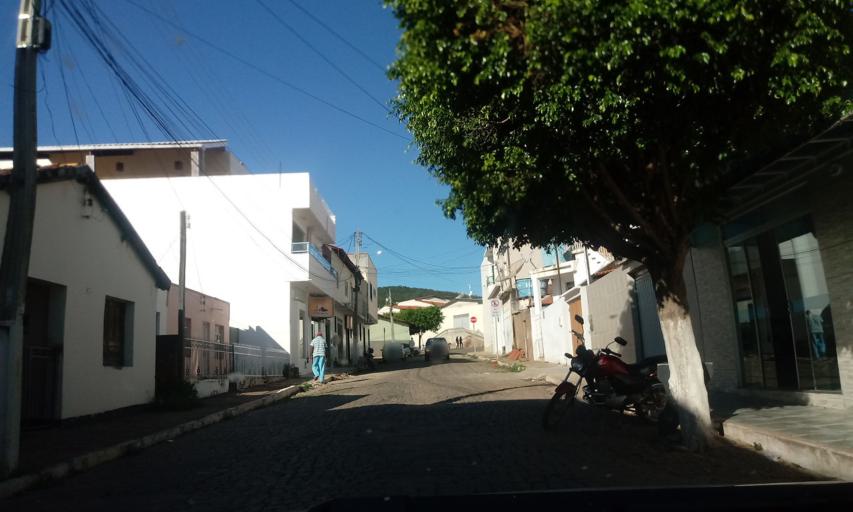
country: BR
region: Bahia
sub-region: Riacho De Santana
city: Riacho de Santana
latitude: -13.7714
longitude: -42.7160
